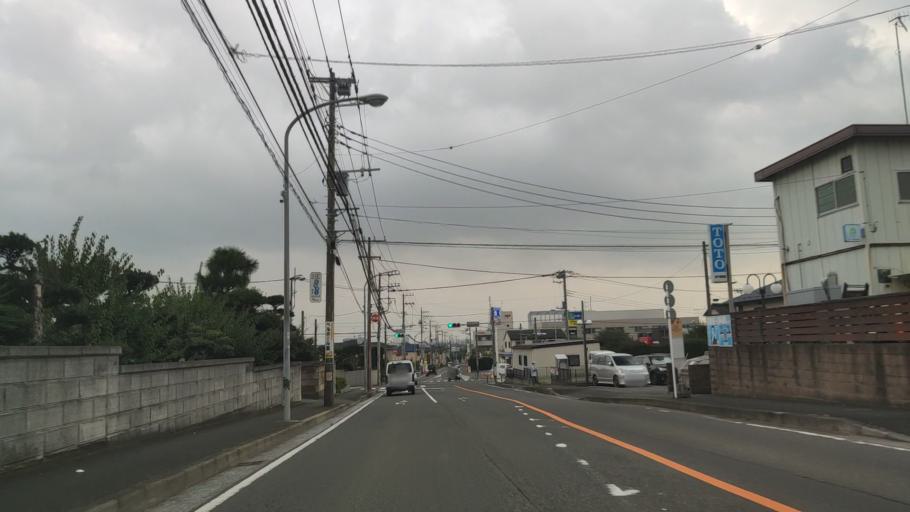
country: JP
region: Kanagawa
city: Minami-rinkan
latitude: 35.4240
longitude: 139.5017
